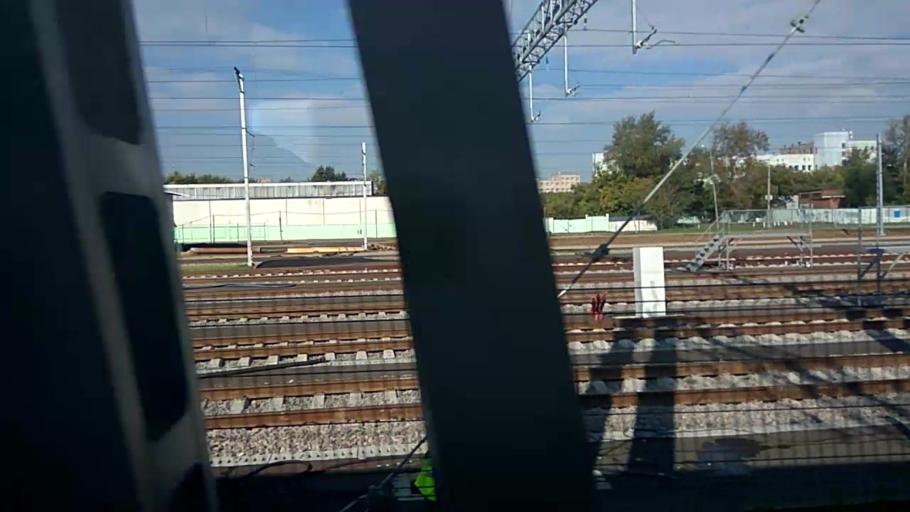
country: RU
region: Moscow
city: Ryazanskiy
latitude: 55.7390
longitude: 37.7330
